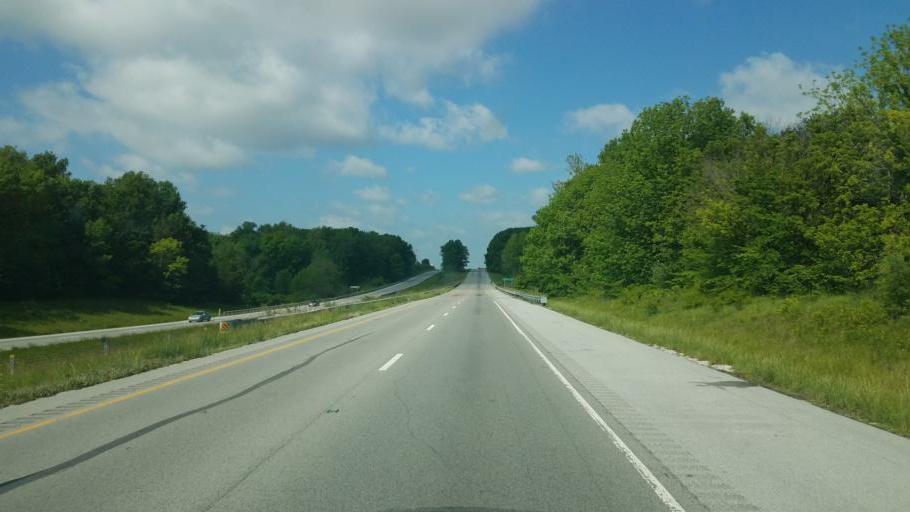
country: US
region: Indiana
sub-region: Putnam County
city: Cloverdale
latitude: 39.5495
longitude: -86.7173
